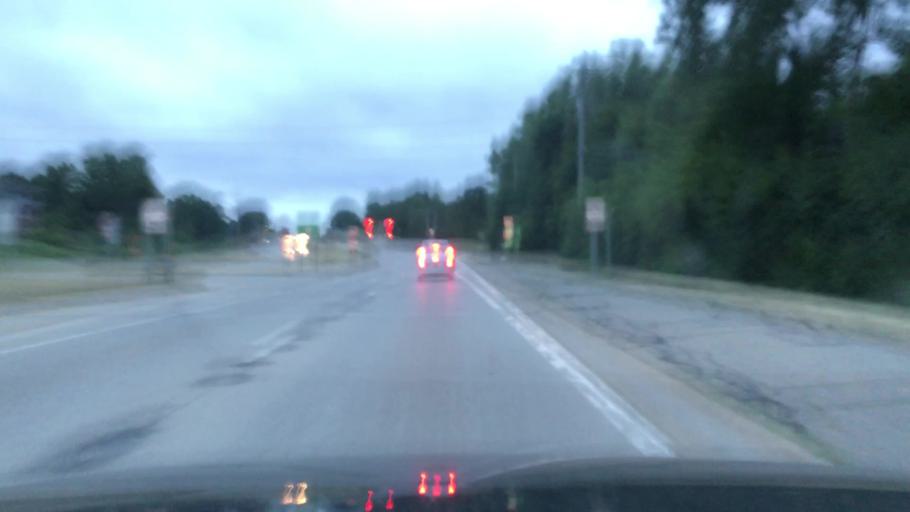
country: US
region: Michigan
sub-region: Kent County
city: East Grand Rapids
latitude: 42.9402
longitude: -85.5853
